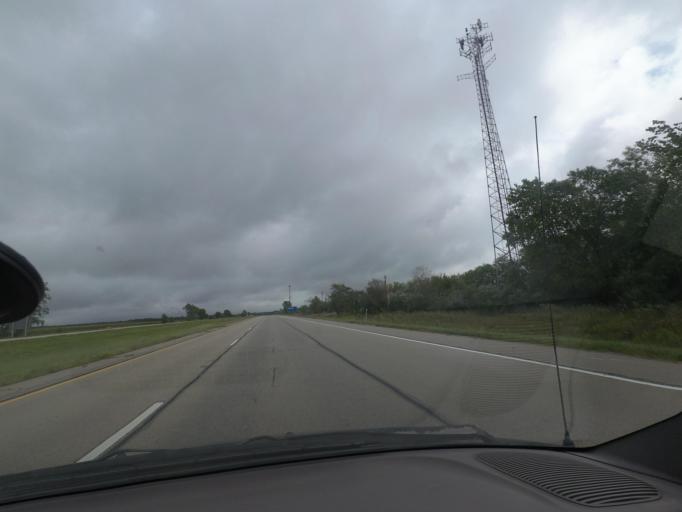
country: US
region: Illinois
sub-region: Piatt County
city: Monticello
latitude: 40.0386
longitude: -88.5920
